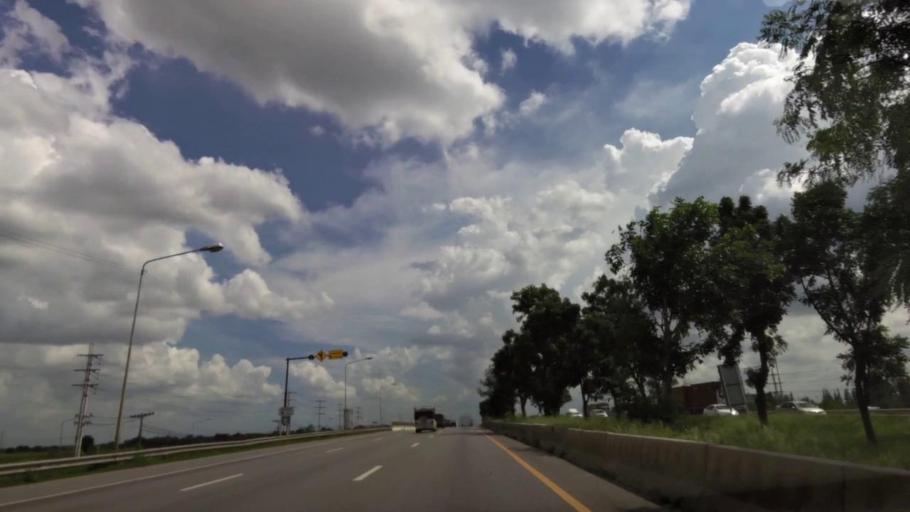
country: TH
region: Phra Nakhon Si Ayutthaya
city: Phra Nakhon Si Ayutthaya
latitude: 14.3874
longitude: 100.6021
